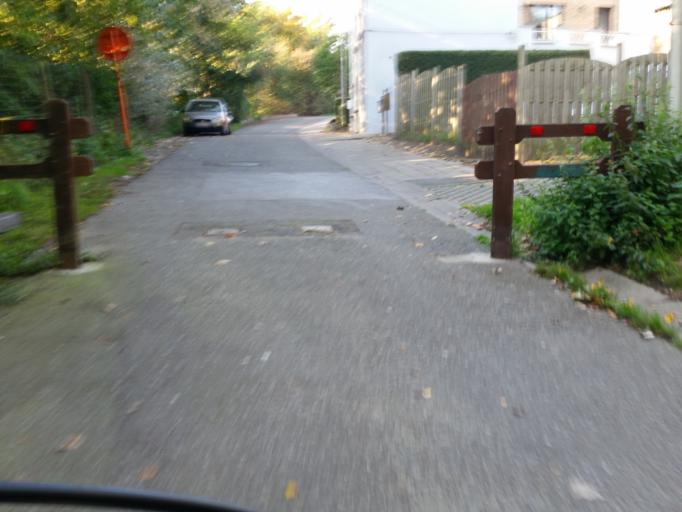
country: BE
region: Flanders
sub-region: Provincie Antwerpen
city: Niel
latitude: 51.1046
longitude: 4.3286
